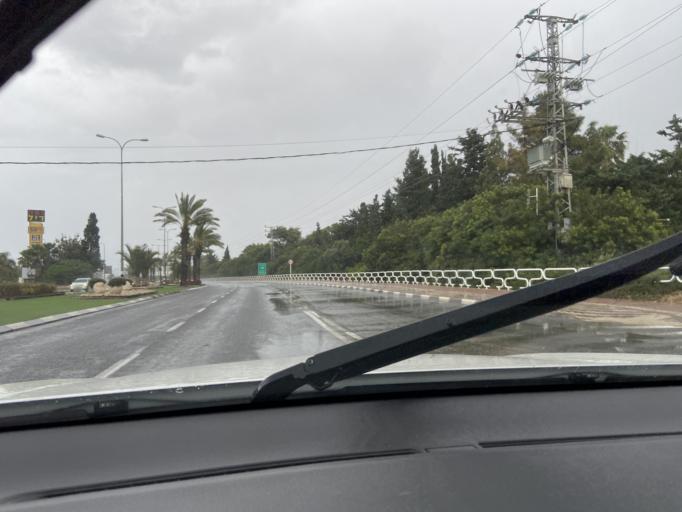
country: IL
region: Northern District
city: El Mazra`a
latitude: 32.9906
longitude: 35.0962
